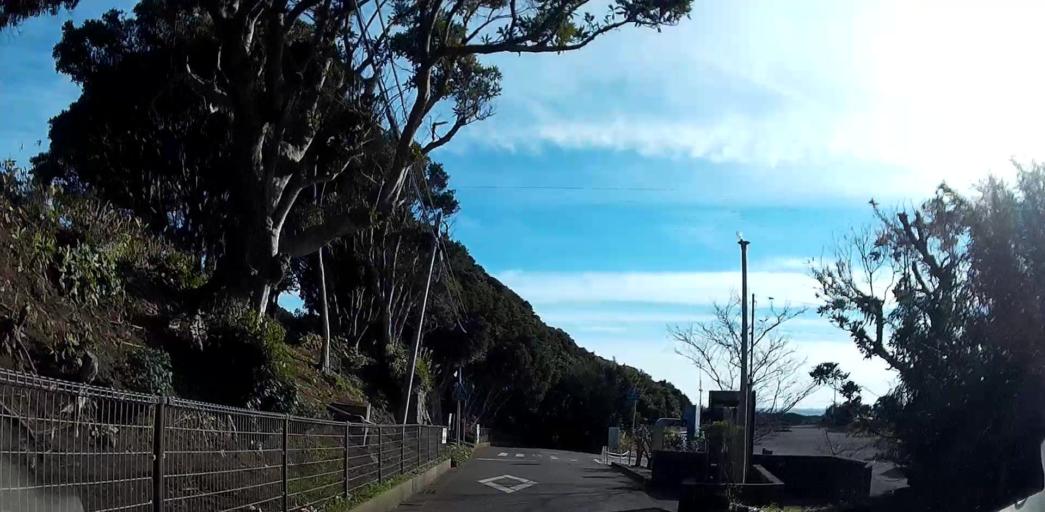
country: JP
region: Chiba
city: Hasaki
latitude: 35.7056
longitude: 140.8522
